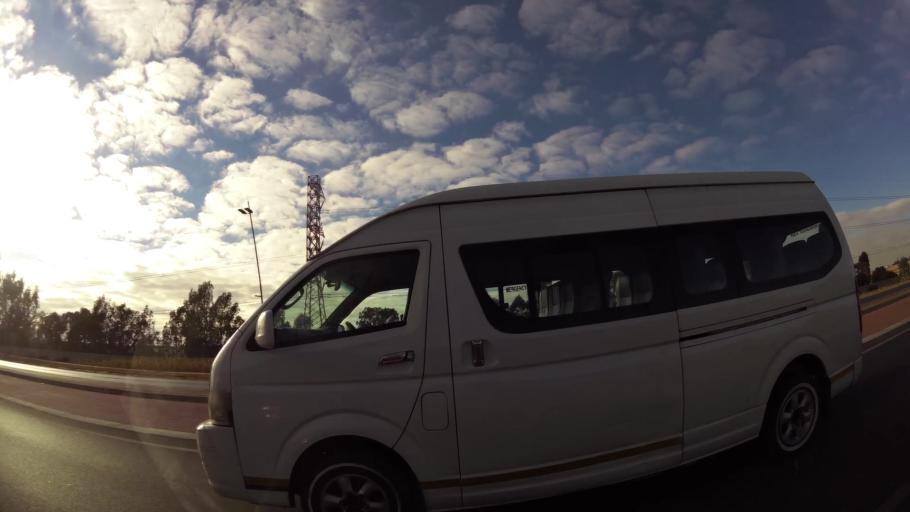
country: ZA
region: Gauteng
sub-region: City of Johannesburg Metropolitan Municipality
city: Modderfontein
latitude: -26.0467
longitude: 28.1868
